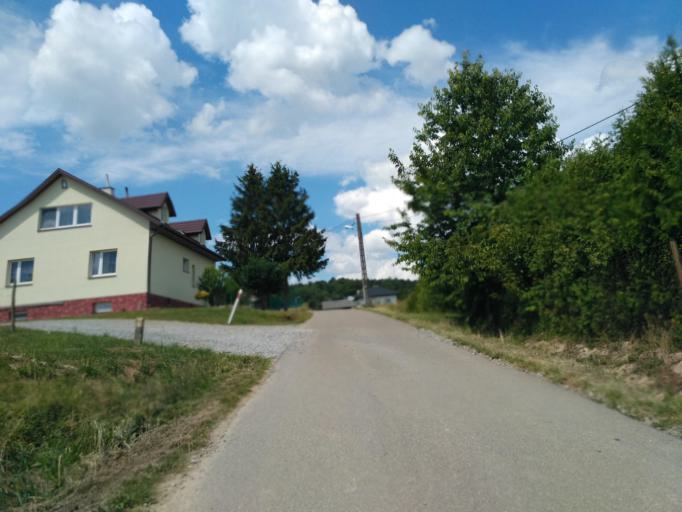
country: PL
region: Subcarpathian Voivodeship
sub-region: Powiat jasielski
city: Brzyska
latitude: 49.8015
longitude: 21.3922
